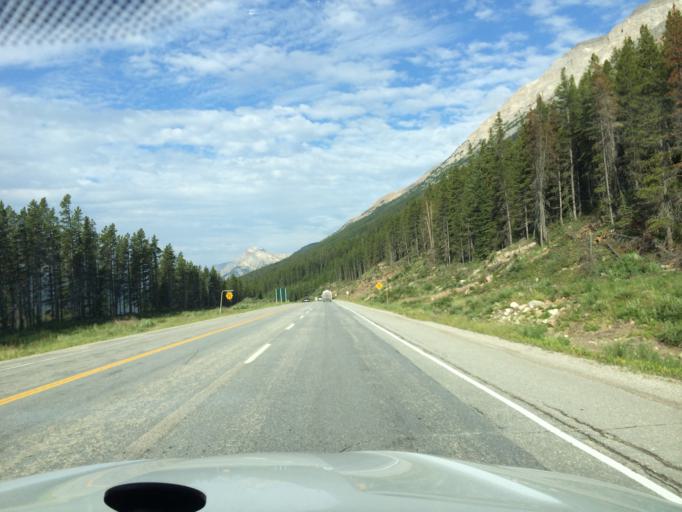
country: CA
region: Alberta
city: Lake Louise
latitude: 51.4524
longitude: -116.3032
